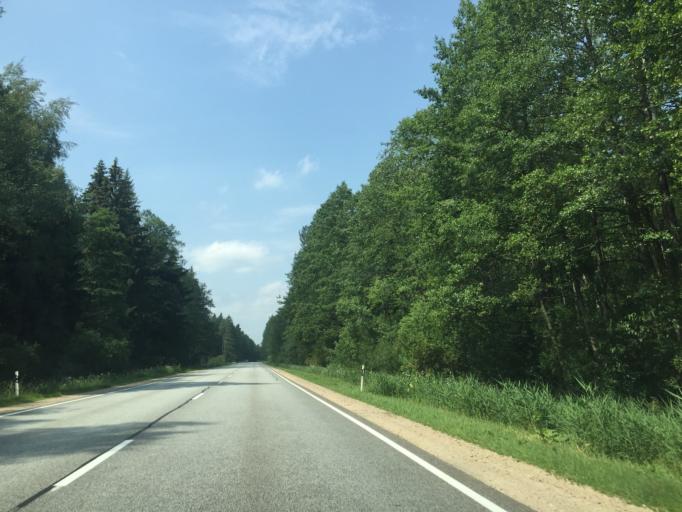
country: LV
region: Kekava
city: Balozi
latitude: 56.8209
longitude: 24.0918
